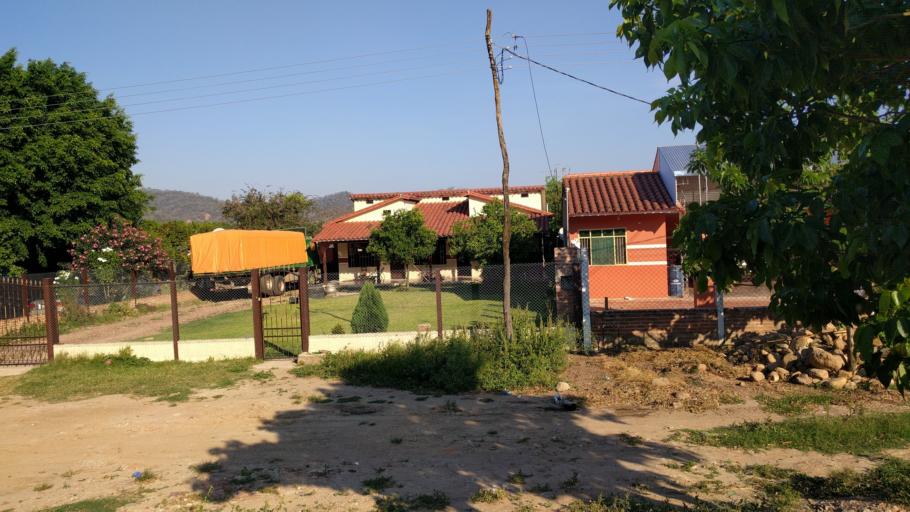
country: BO
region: Santa Cruz
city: Jorochito
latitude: -18.1289
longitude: -63.4681
